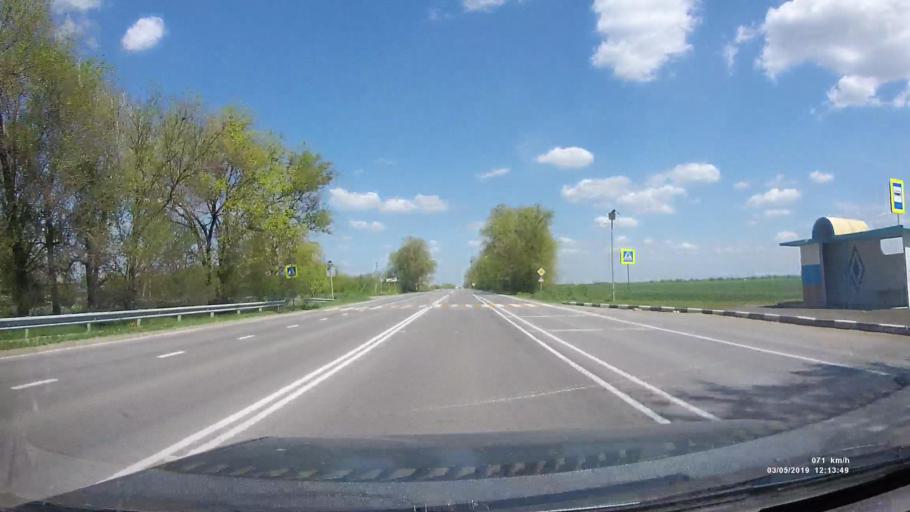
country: RU
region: Rostov
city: Melikhovskaya
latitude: 47.3364
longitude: 40.5577
